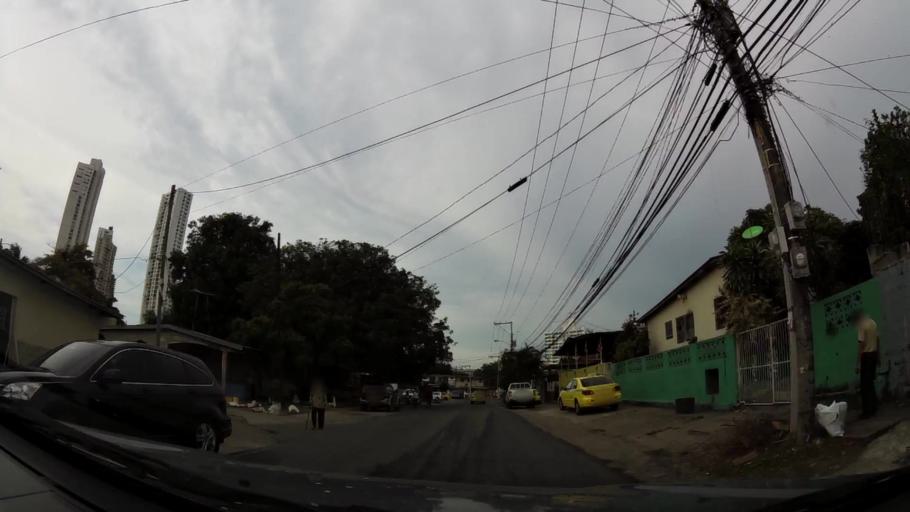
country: PA
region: Panama
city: Panama
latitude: 9.0063
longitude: -79.4940
